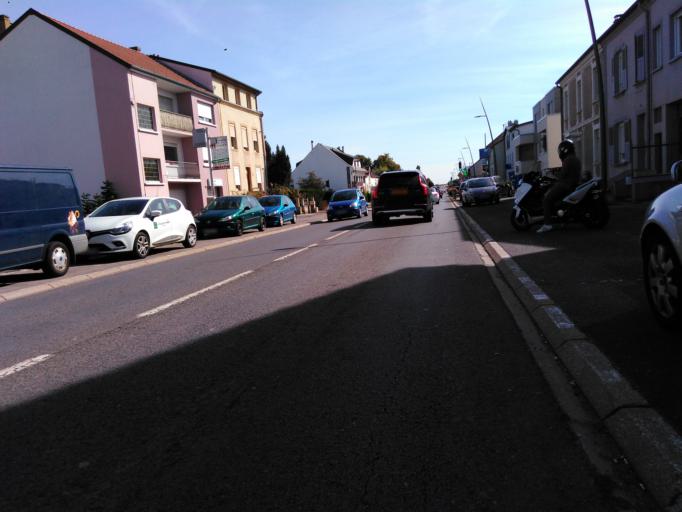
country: FR
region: Lorraine
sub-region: Departement de la Moselle
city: Hettange-Grande
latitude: 49.4024
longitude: 6.1585
